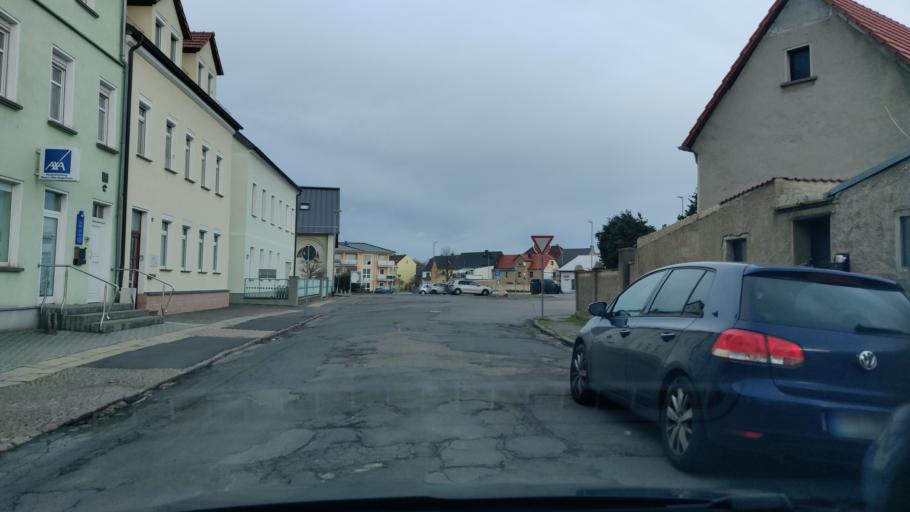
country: DE
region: Saxony
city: Bad Lausick
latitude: 51.1452
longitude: 12.6370
